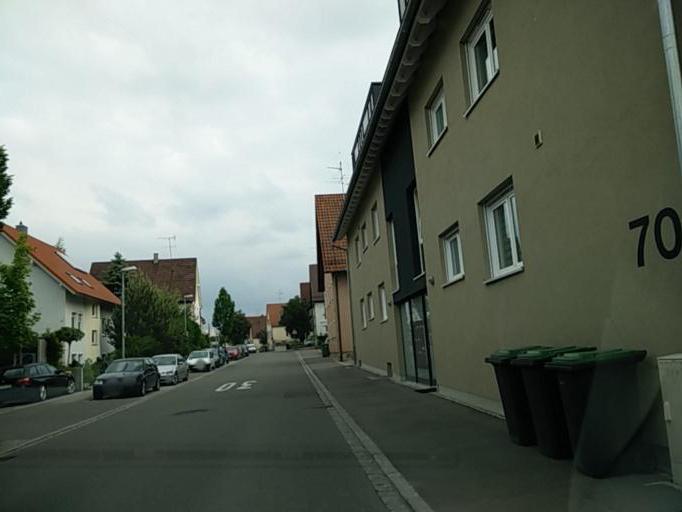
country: DE
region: Baden-Wuerttemberg
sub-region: Regierungsbezirk Stuttgart
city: Holzgerlingen
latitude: 48.6357
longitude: 9.0124
